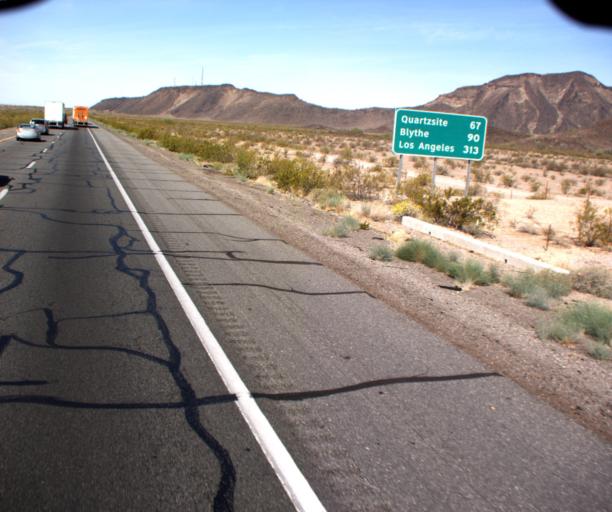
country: US
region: Arizona
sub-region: Maricopa County
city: Buckeye
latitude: 33.5232
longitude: -113.0835
